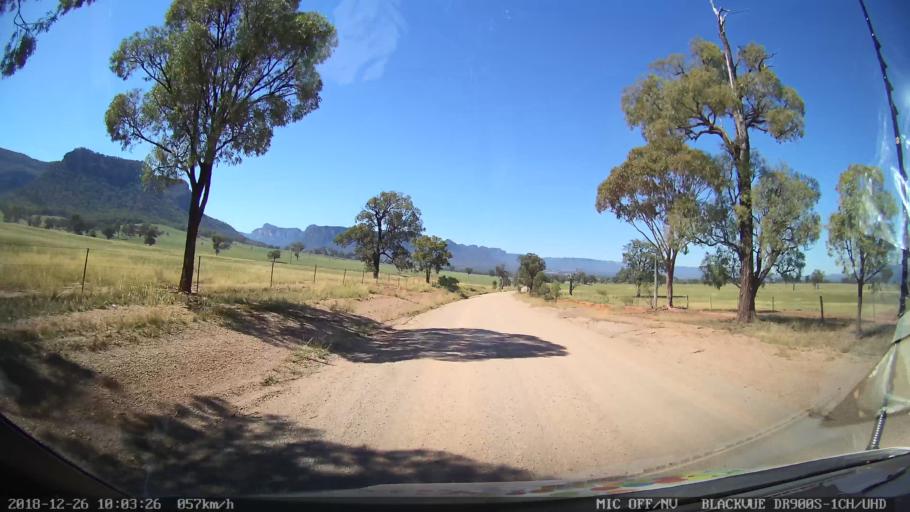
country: AU
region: New South Wales
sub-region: Mid-Western Regional
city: Kandos
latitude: -33.0616
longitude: 150.2178
